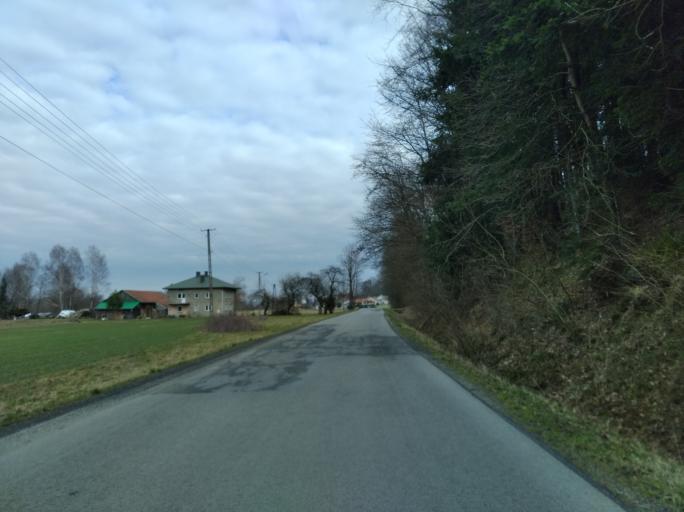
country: PL
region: Subcarpathian Voivodeship
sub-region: Powiat strzyzowski
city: Wisniowa
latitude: 49.8577
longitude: 21.6338
